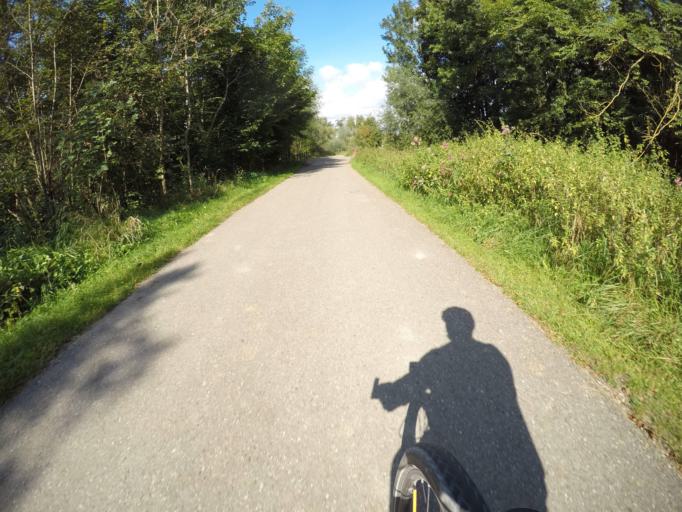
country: DE
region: Bavaria
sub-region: Swabia
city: Schwenningen
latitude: 48.6317
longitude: 10.6503
